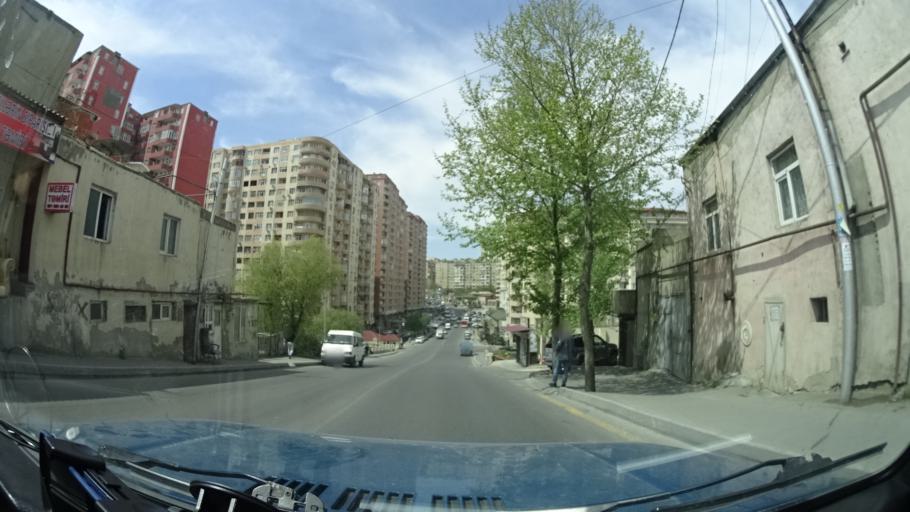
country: AZ
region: Baki
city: Khodzhi-Gasan
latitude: 40.3942
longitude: 49.7978
